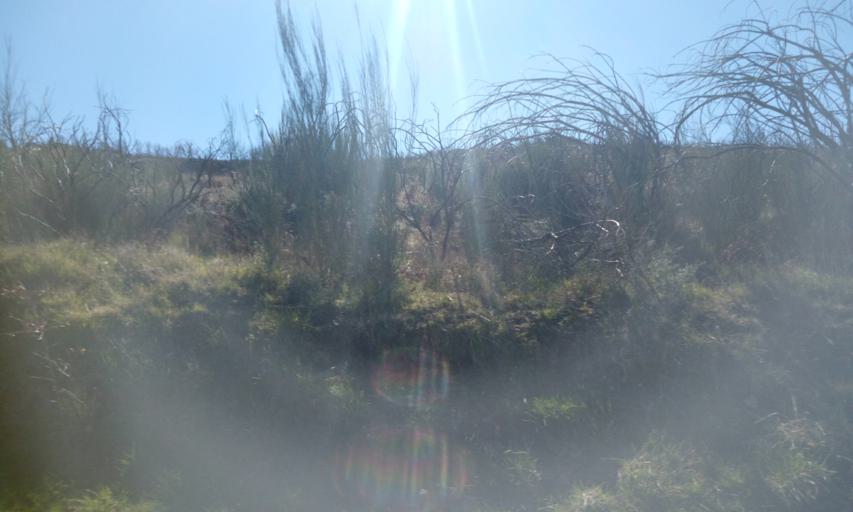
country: PT
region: Guarda
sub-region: Manteigas
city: Manteigas
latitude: 40.4857
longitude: -7.5610
